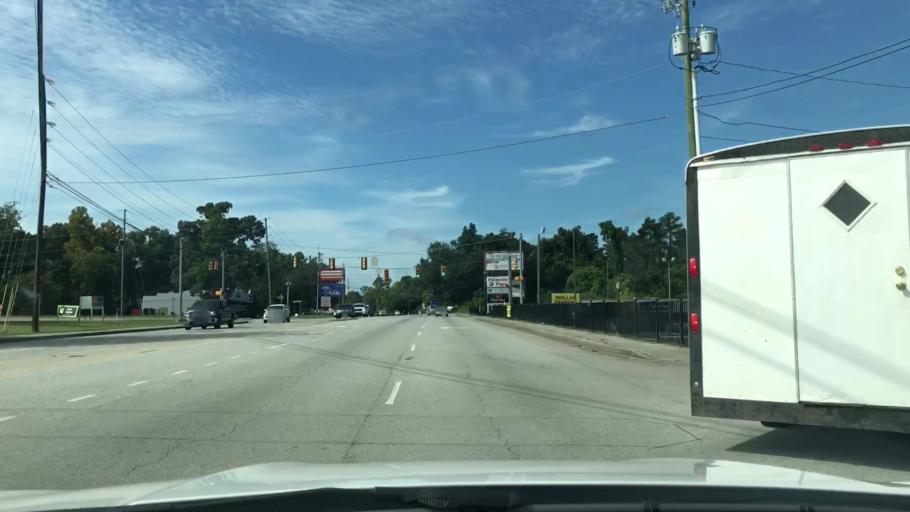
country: US
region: South Carolina
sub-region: Dorchester County
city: Centerville
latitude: 32.9966
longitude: -80.1860
